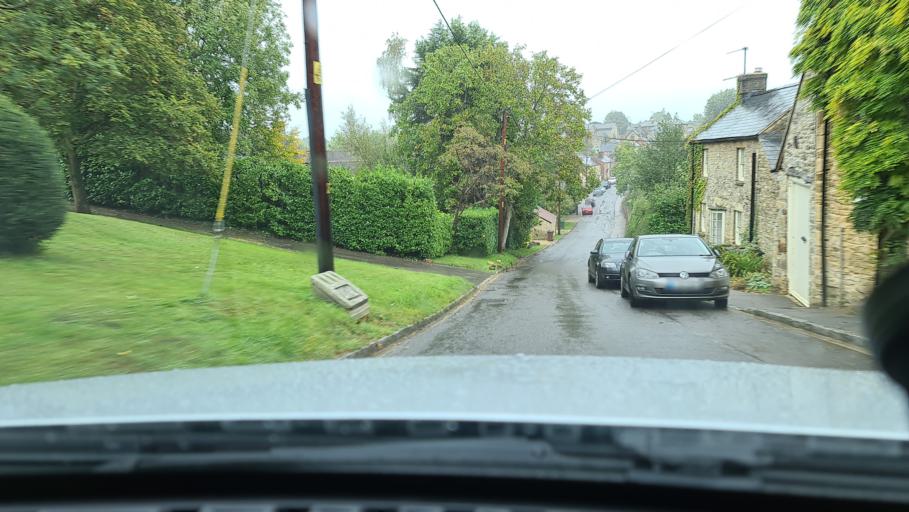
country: GB
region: England
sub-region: Oxfordshire
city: Somerton
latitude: 51.9297
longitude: -1.3085
